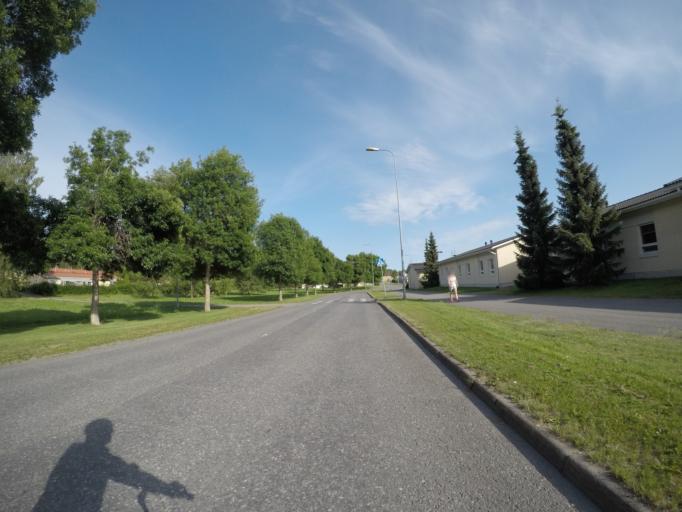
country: FI
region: Haeme
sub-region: Haemeenlinna
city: Haemeenlinna
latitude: 60.9849
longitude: 24.4232
